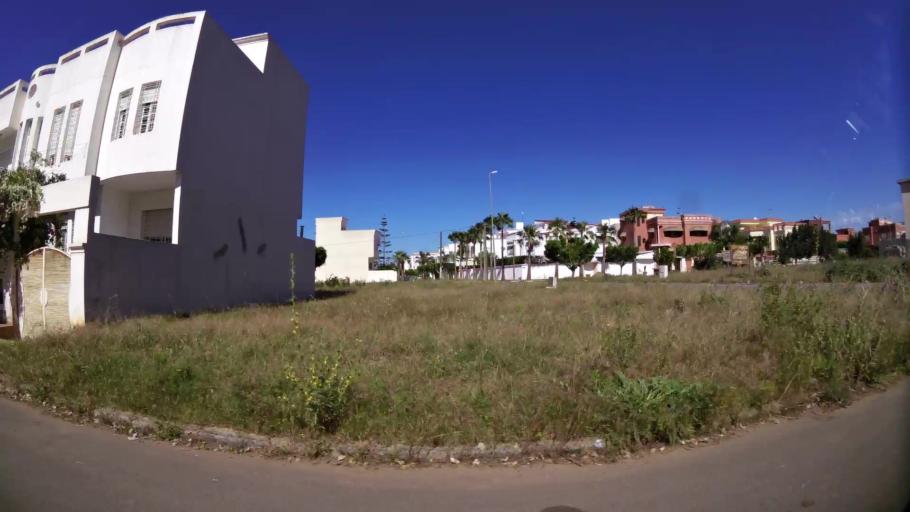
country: MA
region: Oriental
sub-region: Berkane-Taourirt
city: Berkane
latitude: 34.9454
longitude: -2.3290
